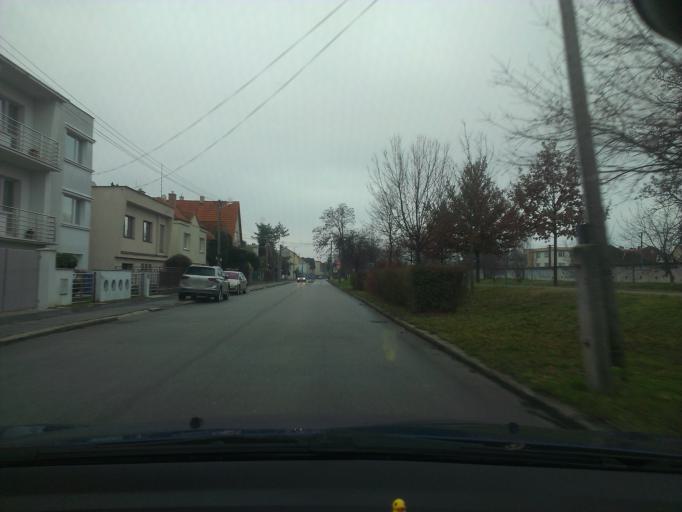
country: SK
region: Trnavsky
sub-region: Okres Trnava
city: Piestany
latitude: 48.5848
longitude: 17.8248
